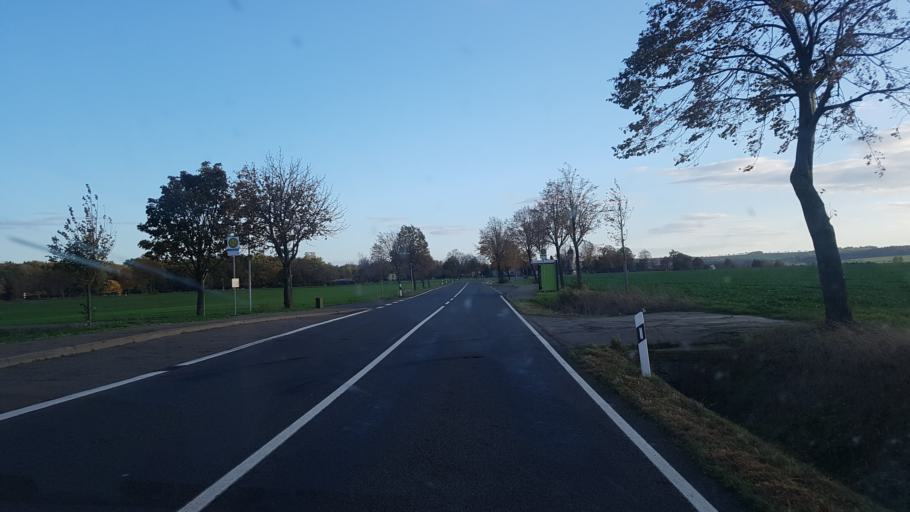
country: DE
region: Saxony
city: Dahlen
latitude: 51.3444
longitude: 13.0298
